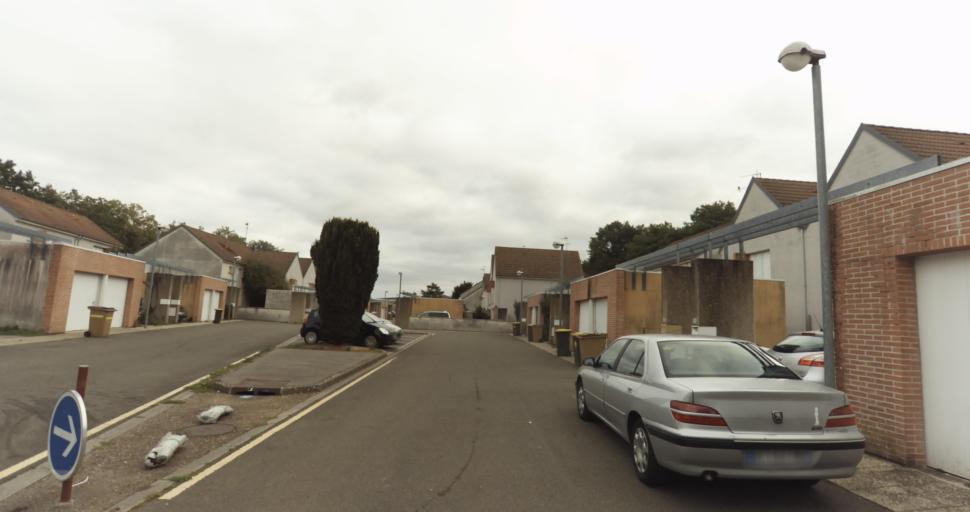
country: FR
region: Centre
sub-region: Departement d'Eure-et-Loir
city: Vernouillet
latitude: 48.7134
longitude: 1.3595
